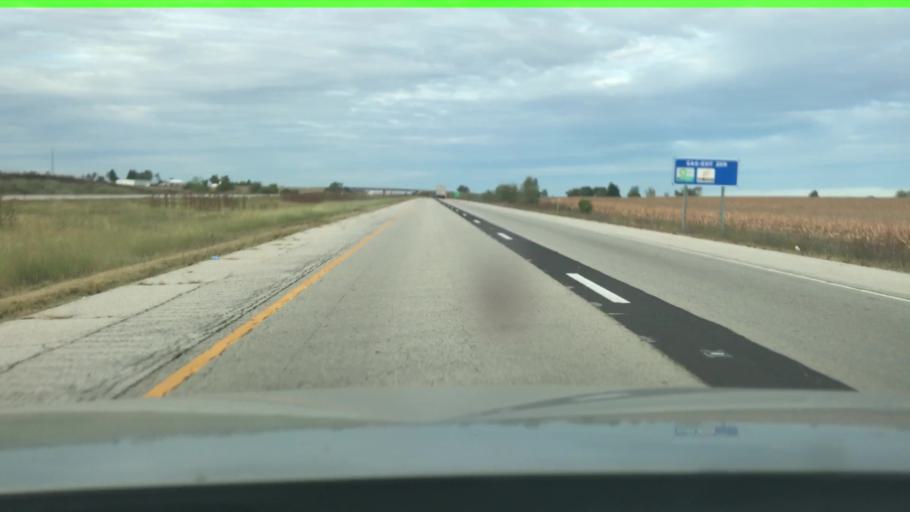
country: US
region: Illinois
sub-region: Livingston County
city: Odell
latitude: 41.0224
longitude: -88.5181
